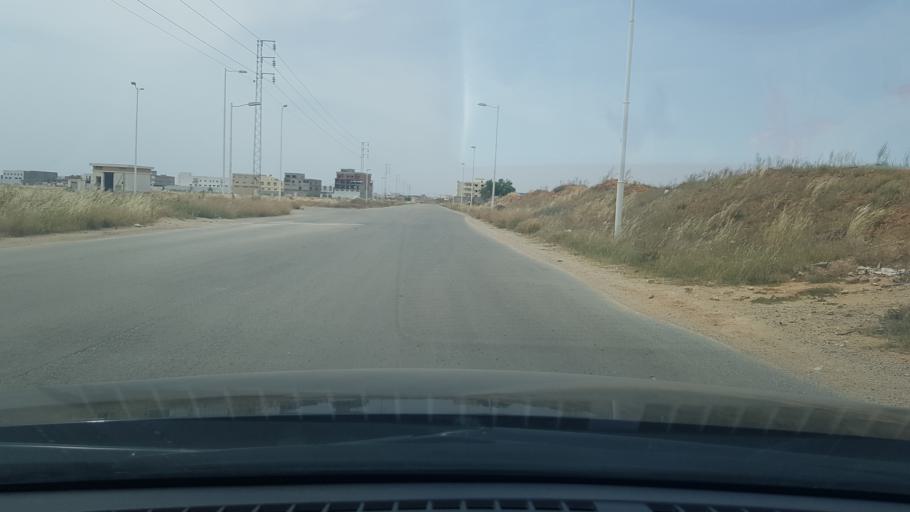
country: TN
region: Safaqis
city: Al Qarmadah
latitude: 34.8312
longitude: 10.7427
